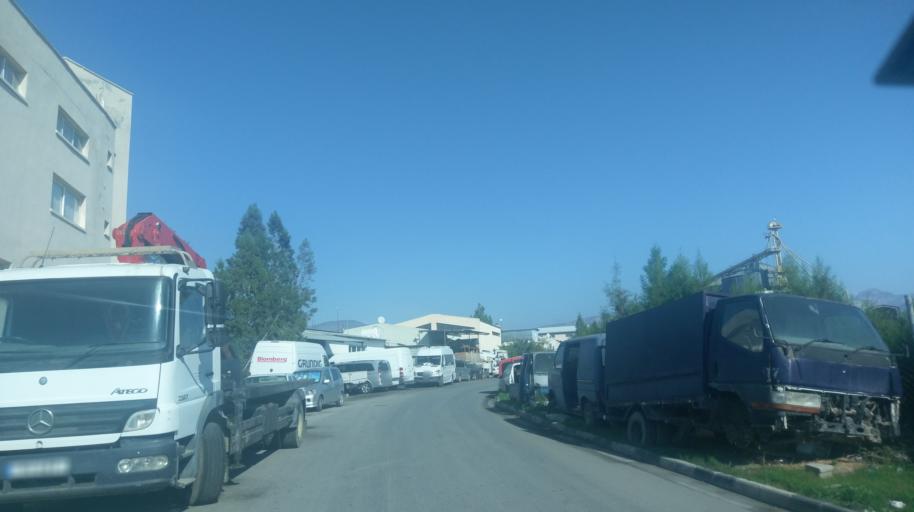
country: CY
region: Lefkosia
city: Nicosia
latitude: 35.2146
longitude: 33.3494
